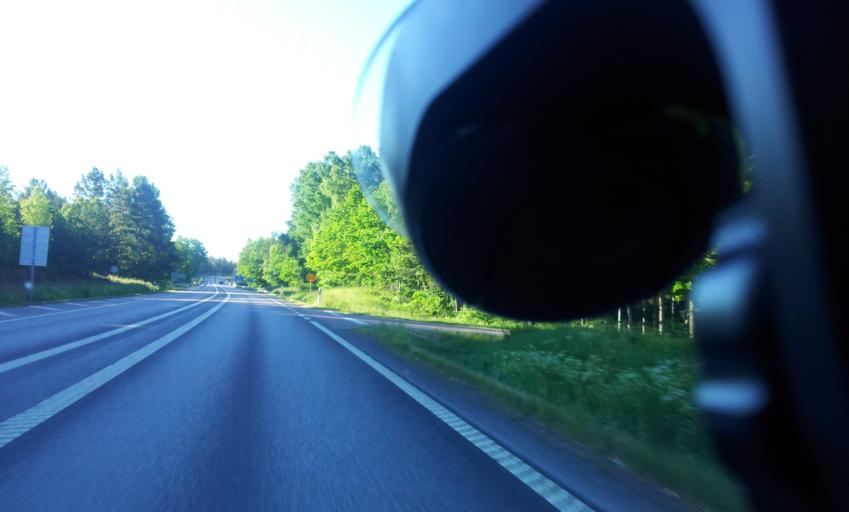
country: SE
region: Kalmar
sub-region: Oskarshamns Kommun
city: Paskallavik
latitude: 57.1282
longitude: 16.4801
